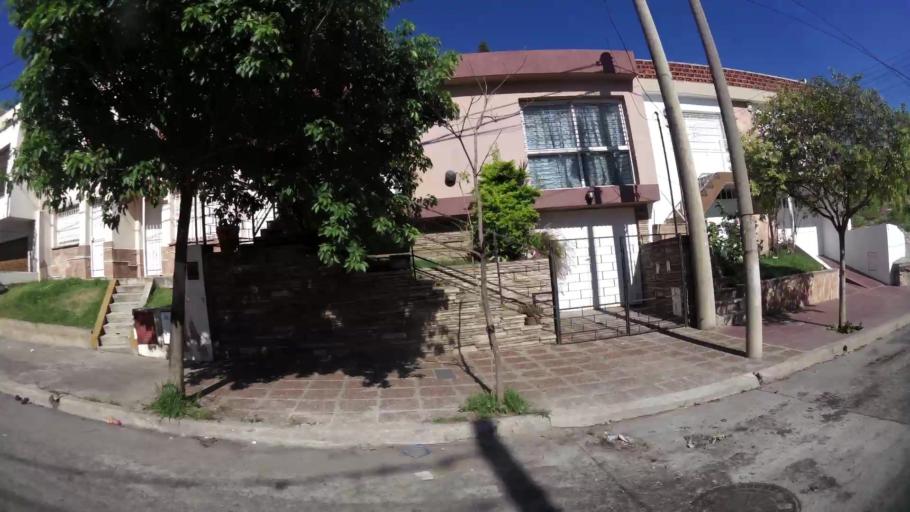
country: AR
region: Cordoba
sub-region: Departamento de Capital
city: Cordoba
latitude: -31.4265
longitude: -64.1625
